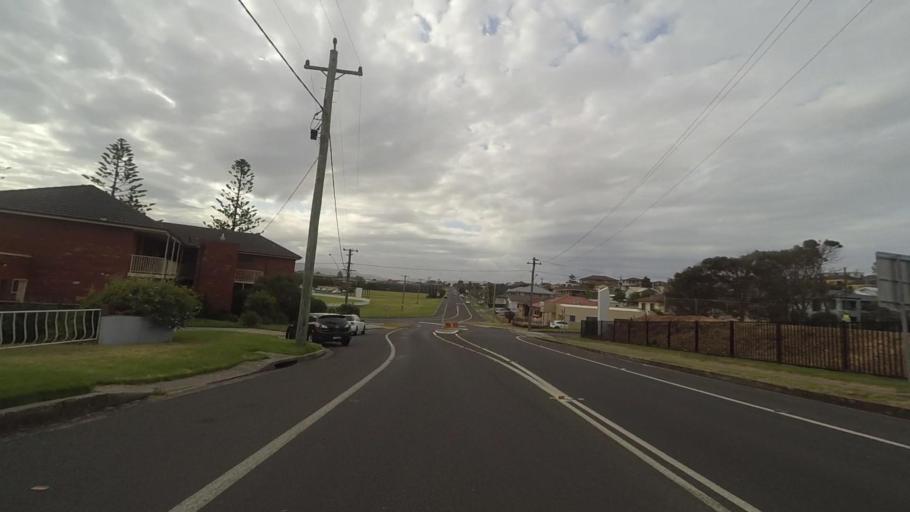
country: AU
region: New South Wales
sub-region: Wollongong
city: Port Kembla
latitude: -34.4898
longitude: 150.9121
